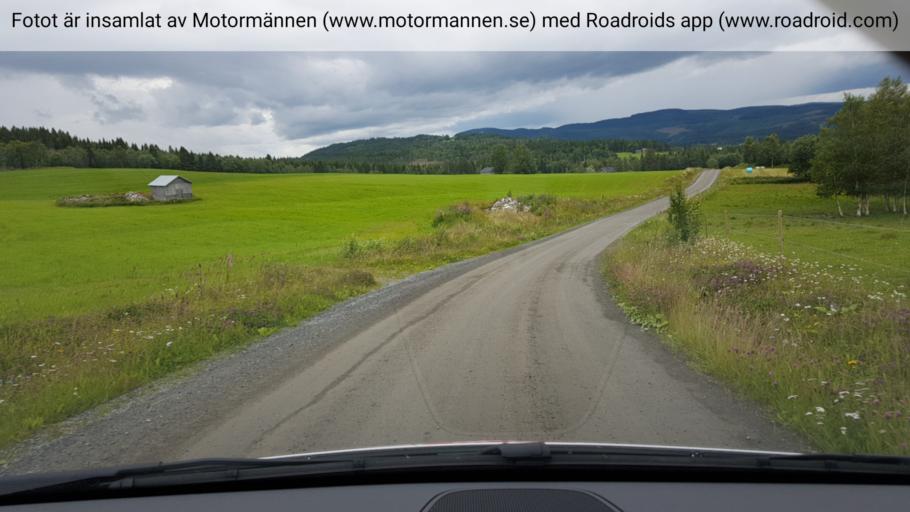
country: SE
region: Jaemtland
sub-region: Krokoms Kommun
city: Valla
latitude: 63.5129
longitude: 13.8966
